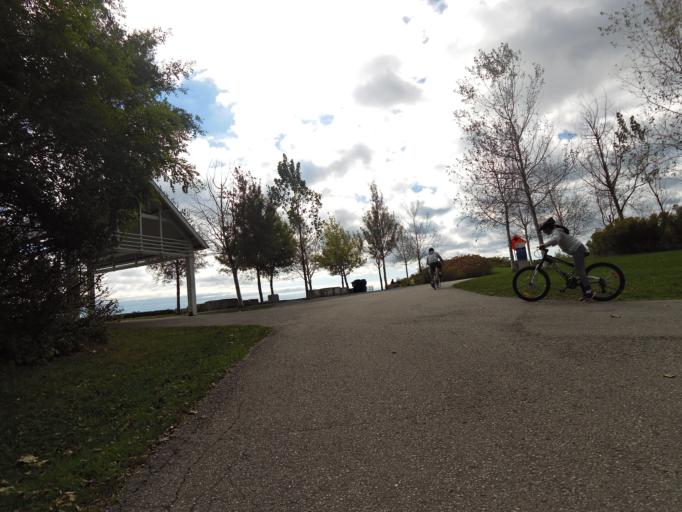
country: CA
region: Ontario
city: Scarborough
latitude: 43.7752
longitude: -79.1341
